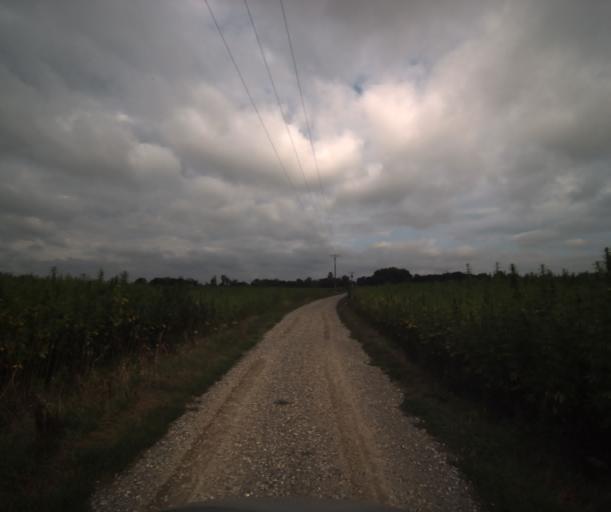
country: FR
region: Midi-Pyrenees
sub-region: Departement de la Haute-Garonne
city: Labastidette
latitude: 43.4460
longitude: 1.2885
